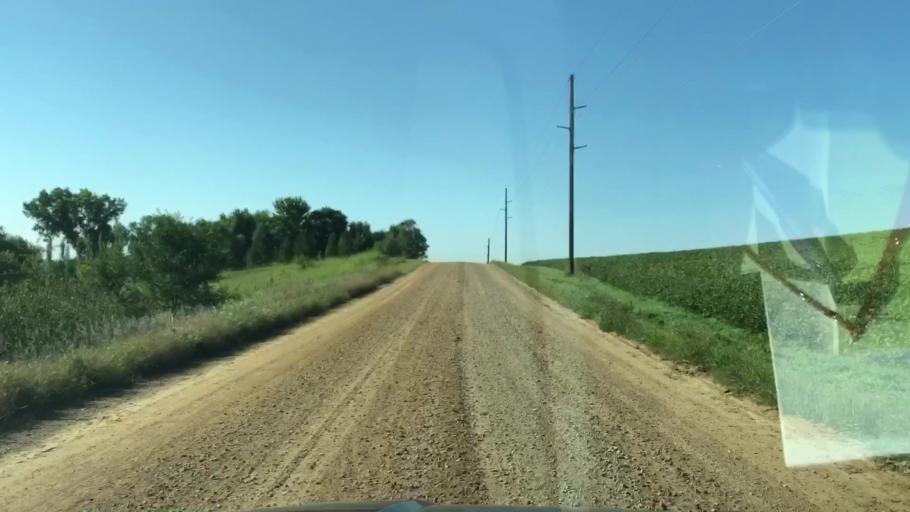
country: US
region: Iowa
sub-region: Woodbury County
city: Sergeant Bluff
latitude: 42.4586
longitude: -96.2527
